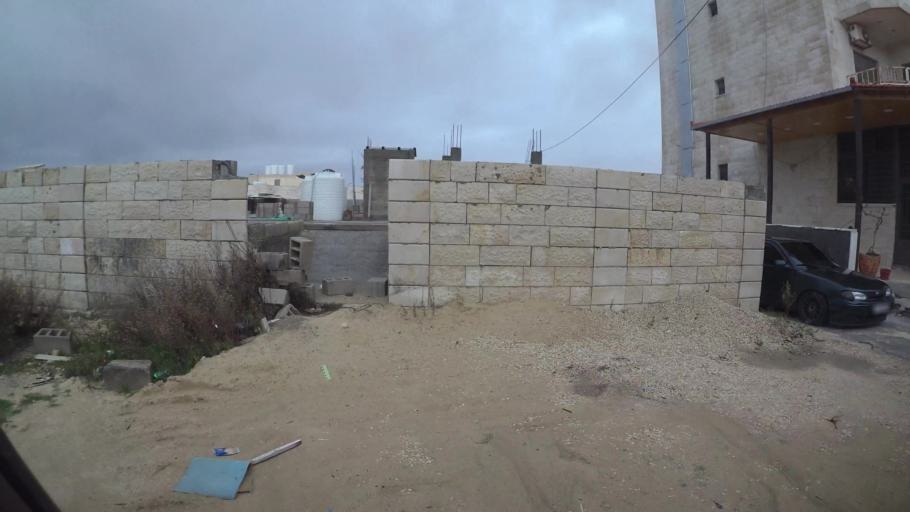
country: JO
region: Amman
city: Al Jubayhah
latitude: 32.0604
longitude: 35.8868
